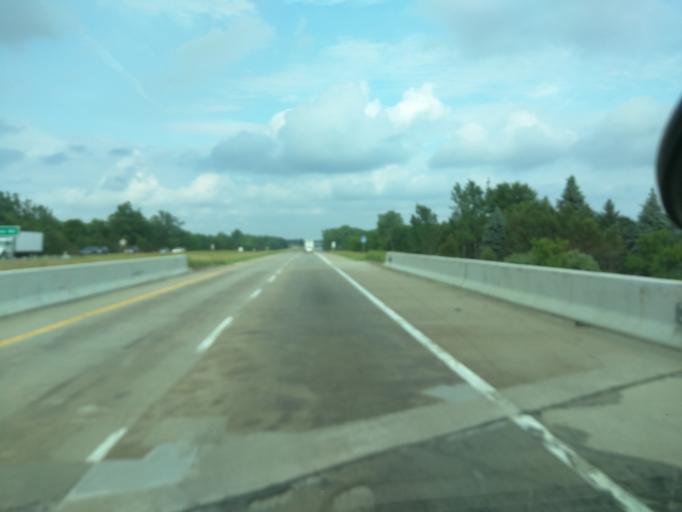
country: US
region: Michigan
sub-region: Clinton County
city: DeWitt
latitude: 42.8169
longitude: -84.5609
